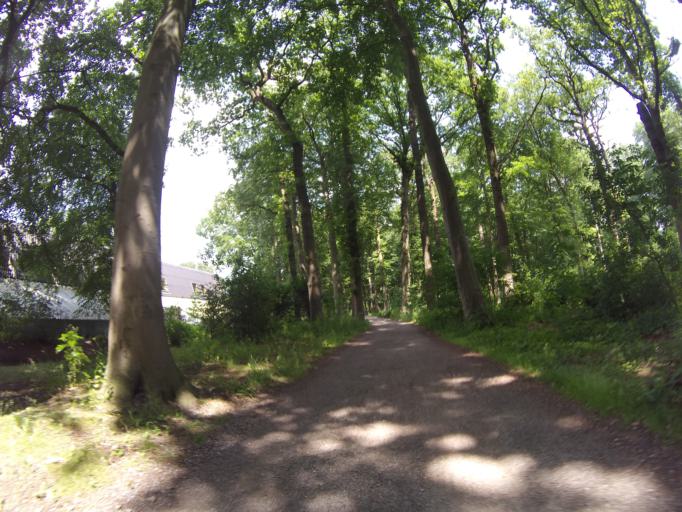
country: NL
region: Utrecht
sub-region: Gemeente De Bilt
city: De Bilt
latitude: 52.1297
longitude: 5.1577
